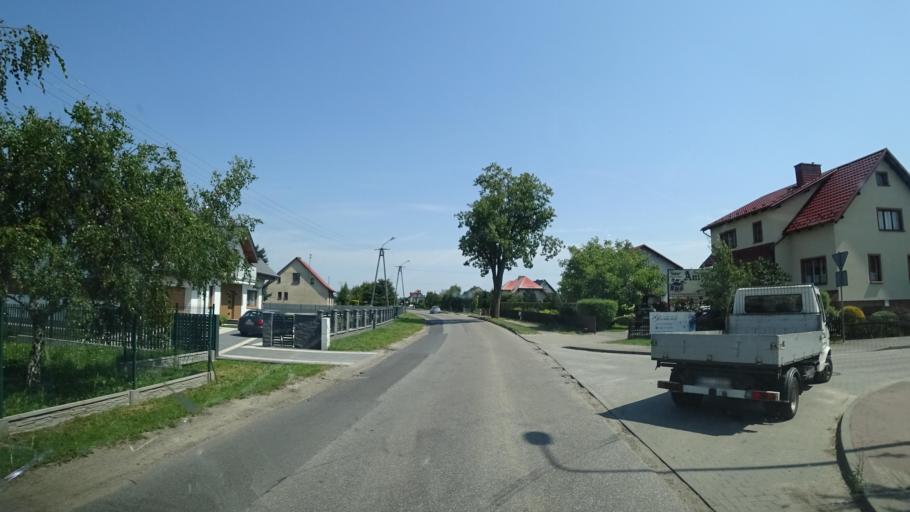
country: PL
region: Pomeranian Voivodeship
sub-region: Powiat chojnicki
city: Brusy
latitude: 53.8839
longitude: 17.7048
